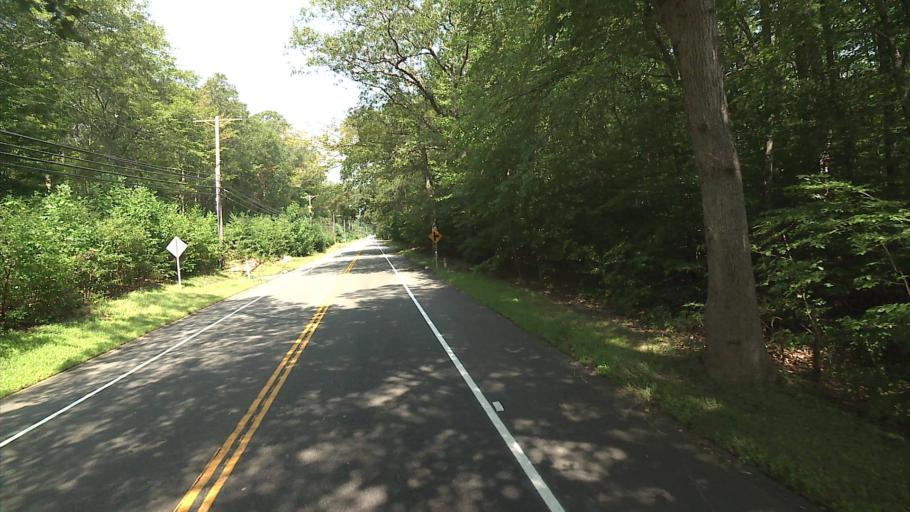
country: US
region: Connecticut
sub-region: New Haven County
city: Madison Center
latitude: 41.3382
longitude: -72.6278
